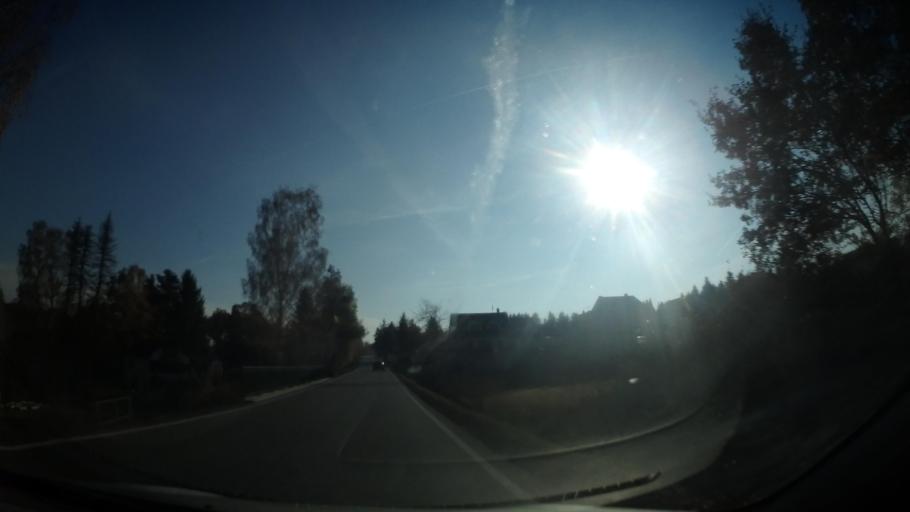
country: CZ
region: Central Bohemia
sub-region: Okres Praha-Vychod
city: Mnichovice
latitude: 49.9153
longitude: 14.7236
